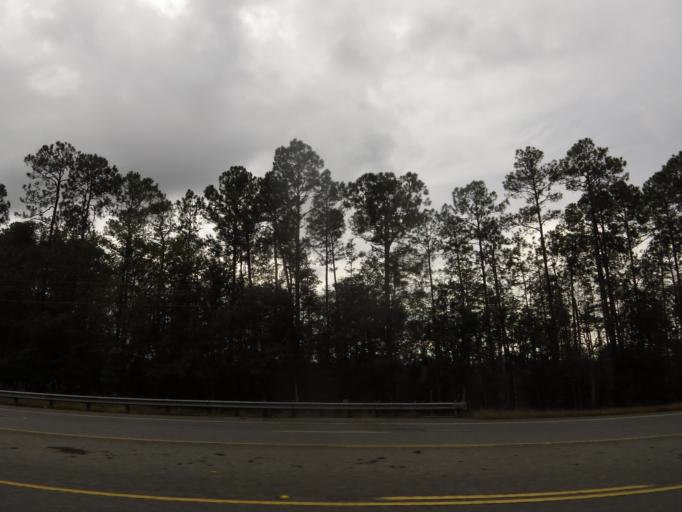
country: US
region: Georgia
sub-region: Wayne County
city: Jesup
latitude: 31.5496
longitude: -81.8115
